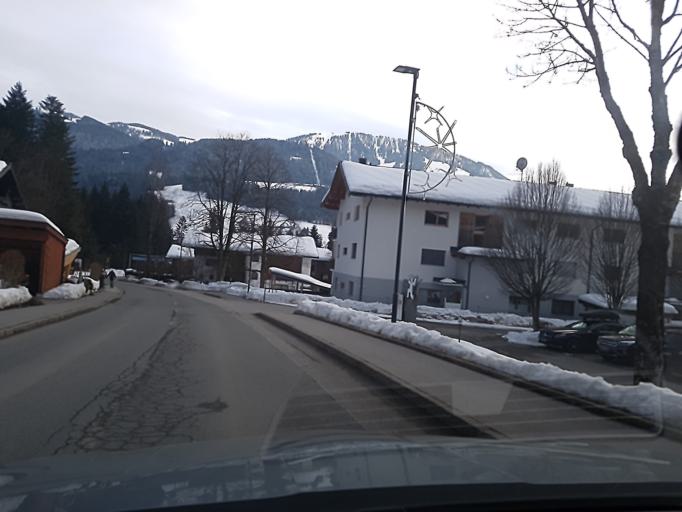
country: AT
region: Tyrol
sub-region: Politischer Bezirk Kufstein
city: Scheffau am Wilden Kaiser
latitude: 47.5260
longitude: 12.2508
